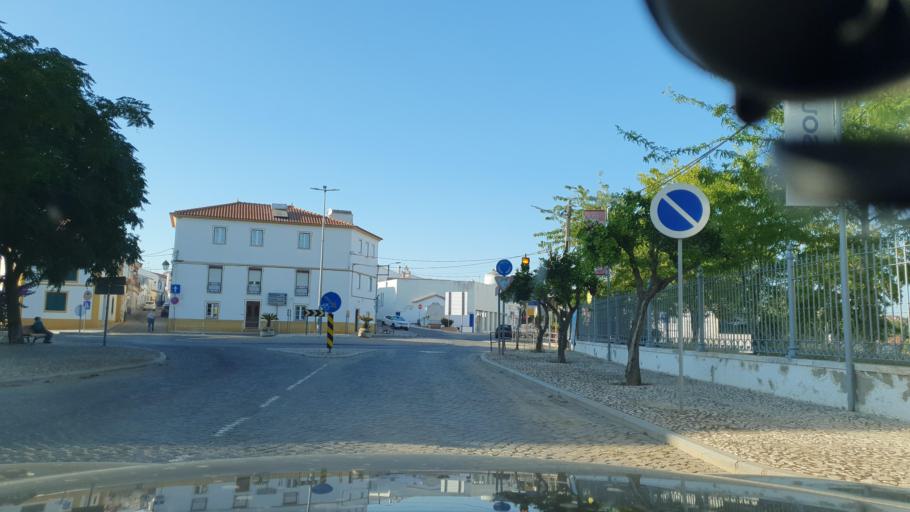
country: PT
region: Portalegre
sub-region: Fronteira
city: Fronteira
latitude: 38.9501
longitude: -7.6758
